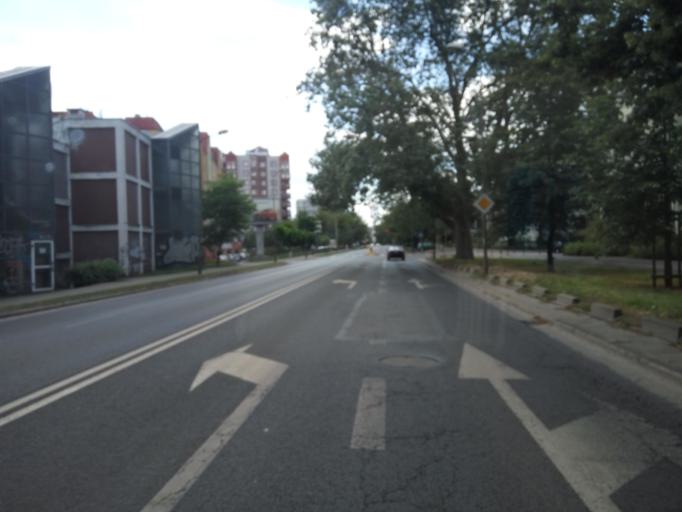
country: PL
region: Lower Silesian Voivodeship
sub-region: Powiat wroclawski
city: Wroclaw
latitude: 51.1166
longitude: 17.0108
